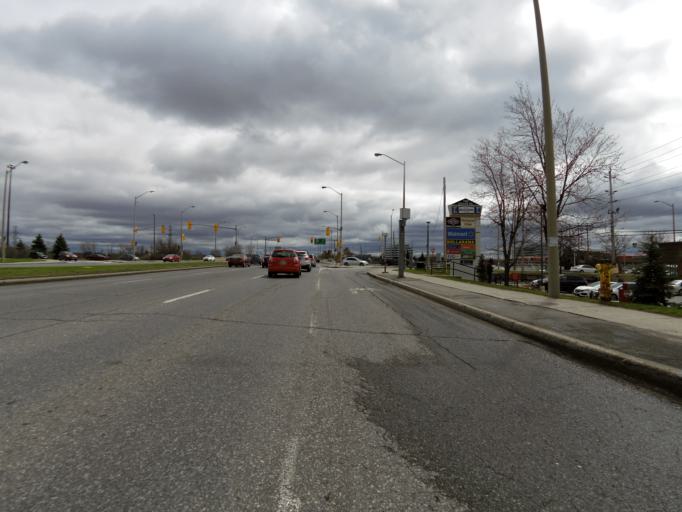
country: CA
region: Ontario
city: Ottawa
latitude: 45.4337
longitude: -75.6082
